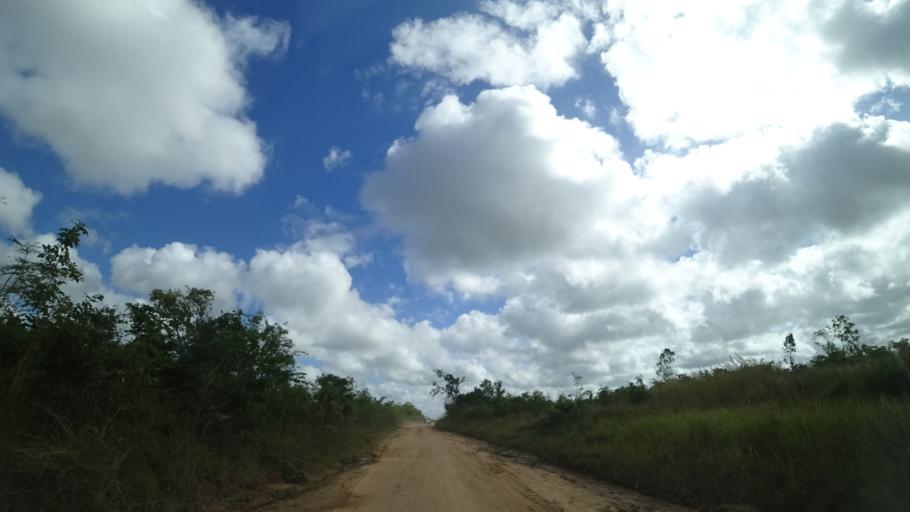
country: MZ
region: Sofala
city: Dondo
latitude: -19.4438
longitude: 34.7160
